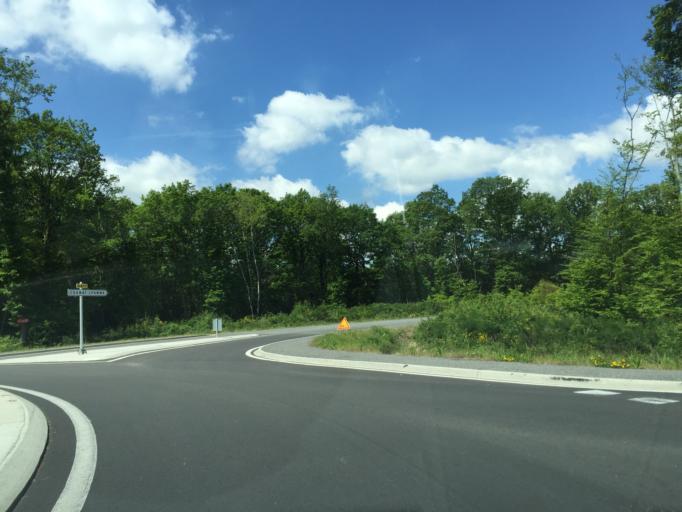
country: FR
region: Auvergne
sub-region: Departement de l'Allier
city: Brugheas
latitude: 46.0962
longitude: 3.3482
